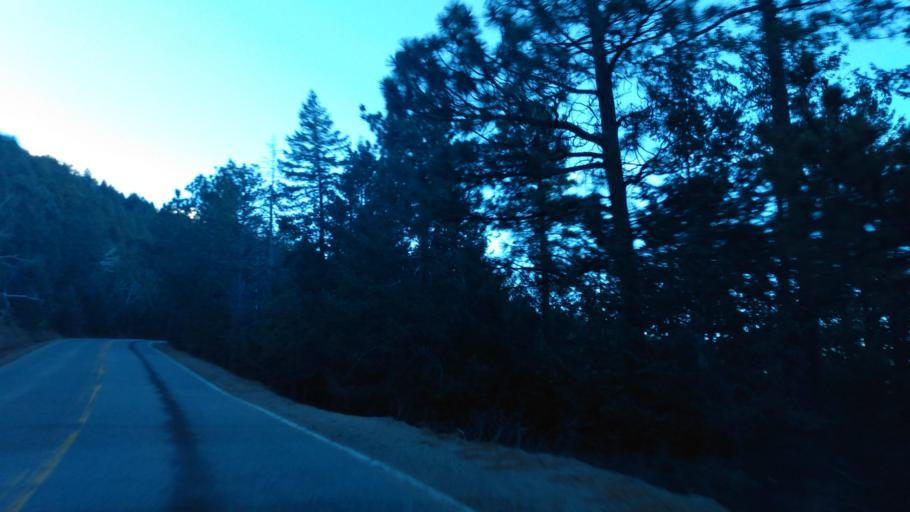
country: US
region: Colorado
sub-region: Boulder County
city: Coal Creek
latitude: 39.9849
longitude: -105.3754
